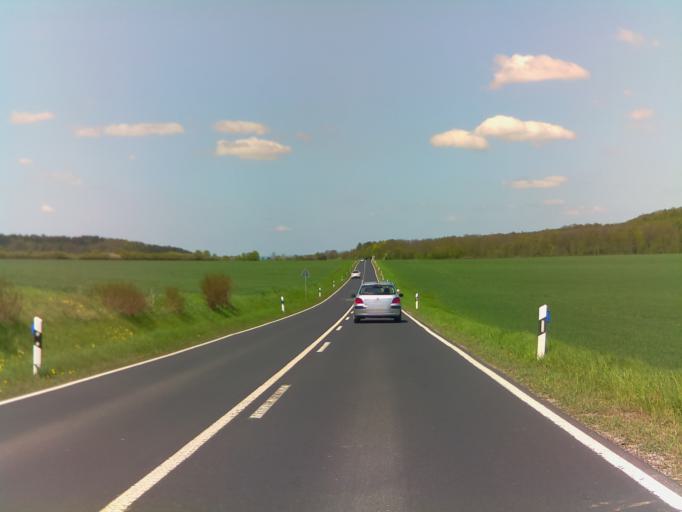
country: DE
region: Thuringia
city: Dornheim
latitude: 50.8019
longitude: 10.9815
